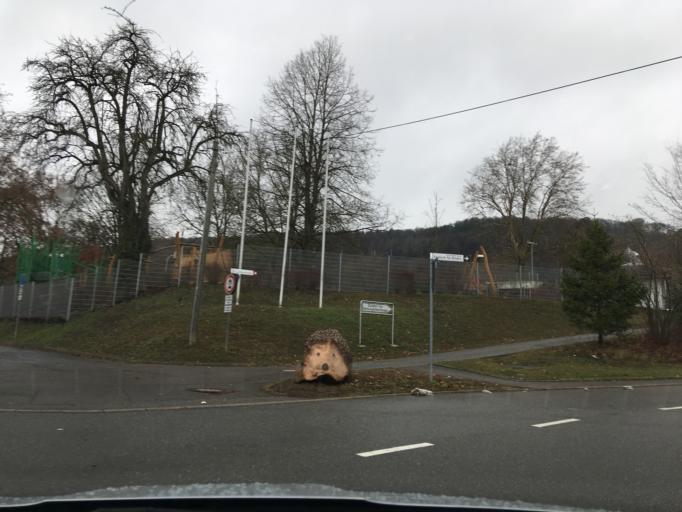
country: DE
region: Baden-Wuerttemberg
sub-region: Freiburg Region
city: Gottmadingen
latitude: 47.7388
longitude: 8.7680
